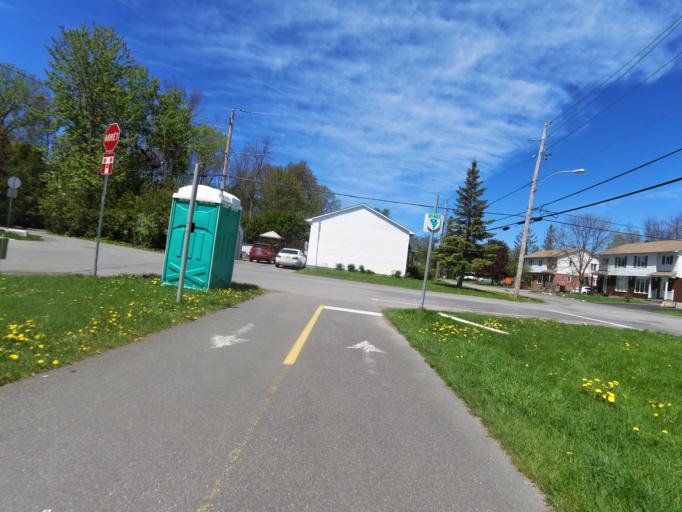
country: CA
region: Ontario
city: Bells Corners
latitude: 45.4047
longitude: -75.8728
